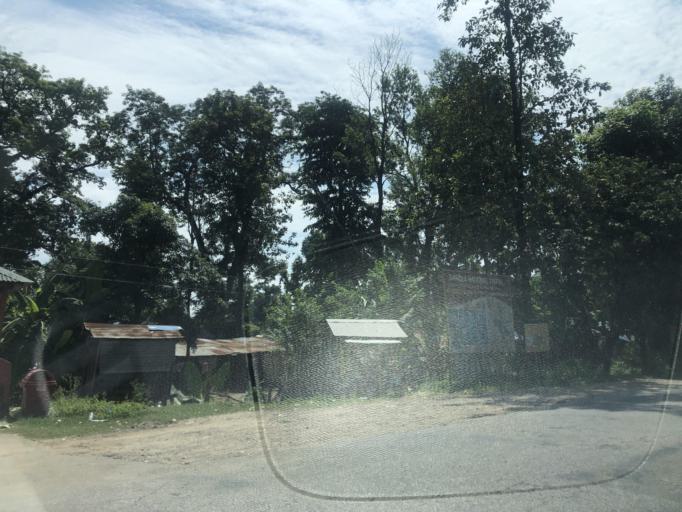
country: NP
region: Far Western
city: Tikapur
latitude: 28.5108
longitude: 81.3251
